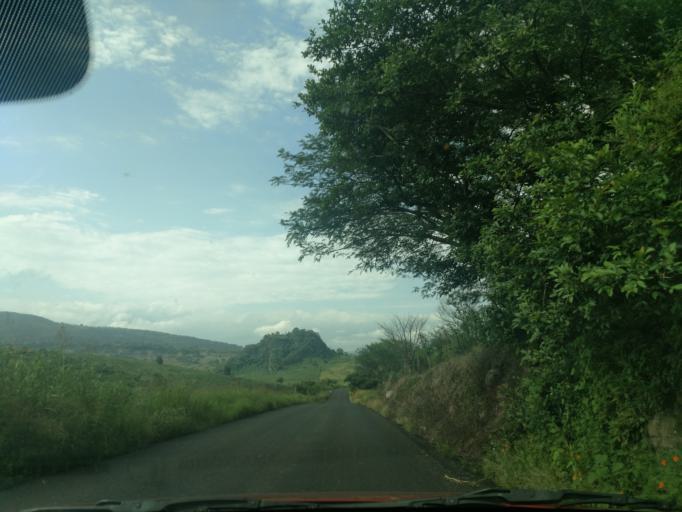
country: MX
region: Jalisco
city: El Salto
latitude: 20.4357
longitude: -104.4723
